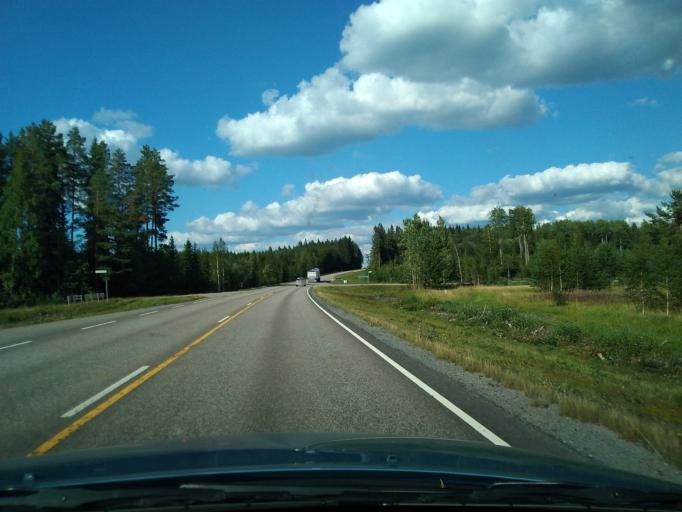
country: FI
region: Pirkanmaa
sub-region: Ylae-Pirkanmaa
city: Maenttae
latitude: 62.0974
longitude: 24.7293
